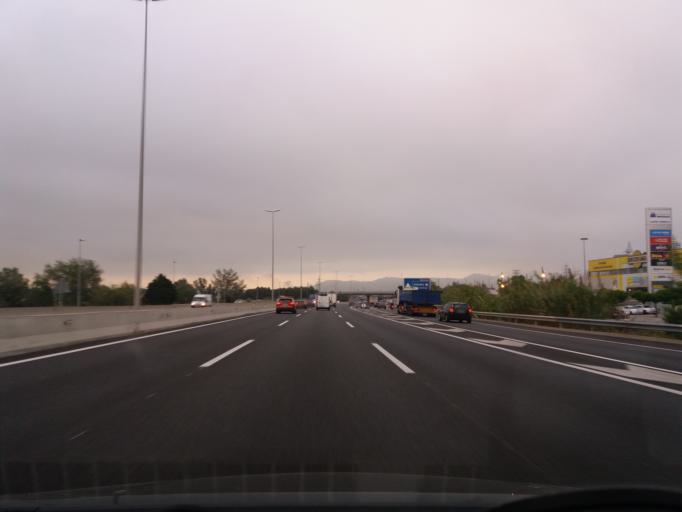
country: ES
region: Catalonia
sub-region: Provincia de Barcelona
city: Abrera
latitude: 41.5077
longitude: 1.9036
